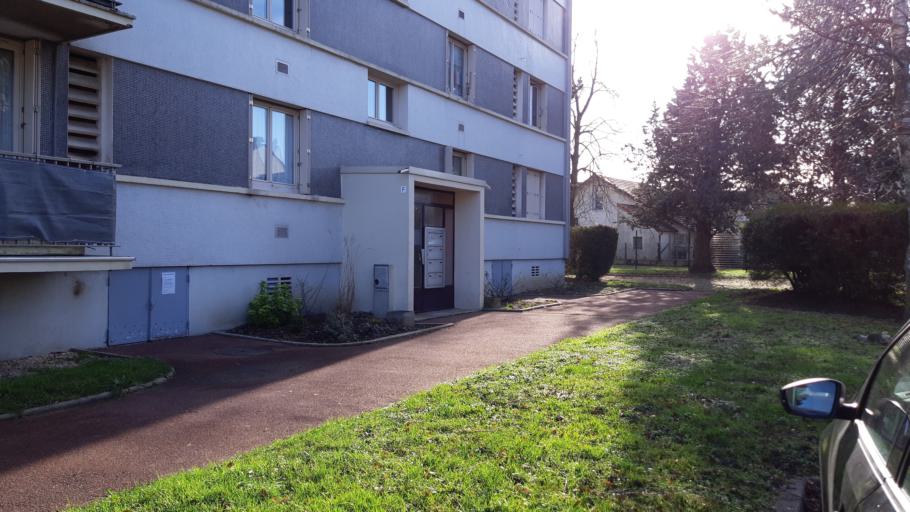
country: FR
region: Ile-de-France
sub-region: Departement de l'Essonne
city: Bretigny-sur-Orge
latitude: 48.6019
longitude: 2.2956
